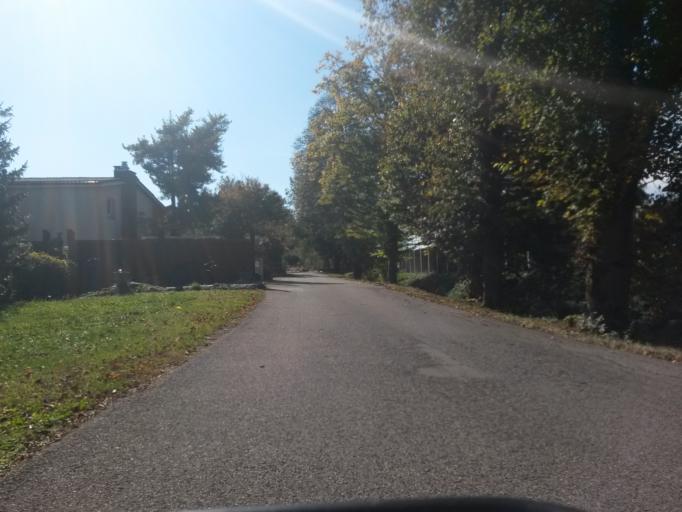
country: CH
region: Solothurn
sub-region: Bezirk Wasseramt
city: Deitingen
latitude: 47.2257
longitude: 7.6174
